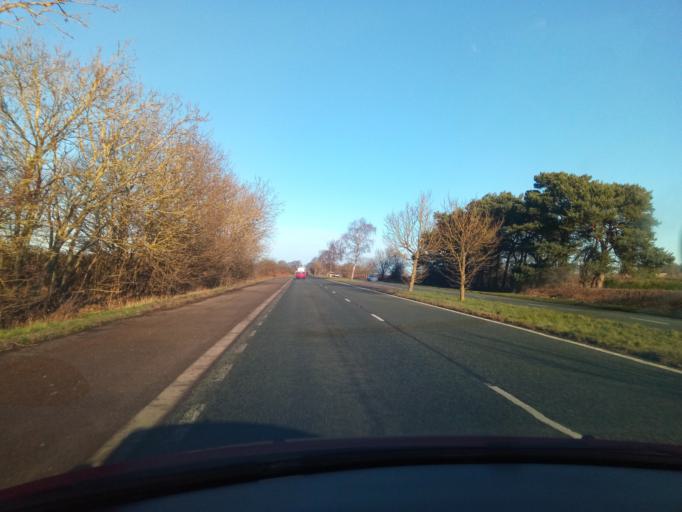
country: GB
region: England
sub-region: Nottinghamshire
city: Farnsfield
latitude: 53.0626
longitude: -1.0705
